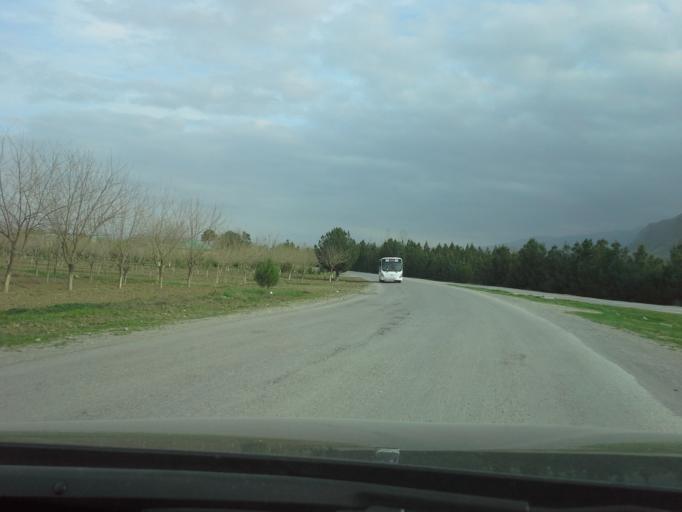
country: TM
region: Ahal
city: Abadan
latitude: 37.9371
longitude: 58.2231
